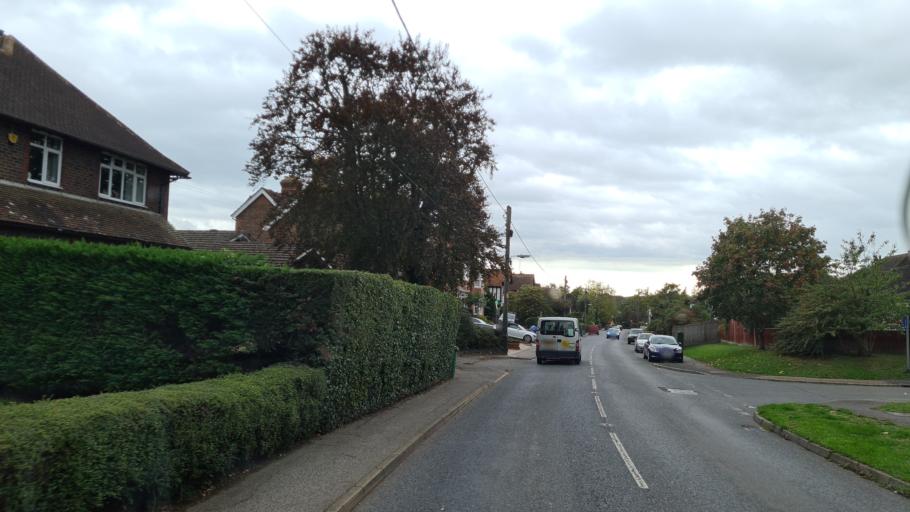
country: GB
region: England
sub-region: West Sussex
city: Partridge Green
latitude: 50.9871
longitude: -0.2730
